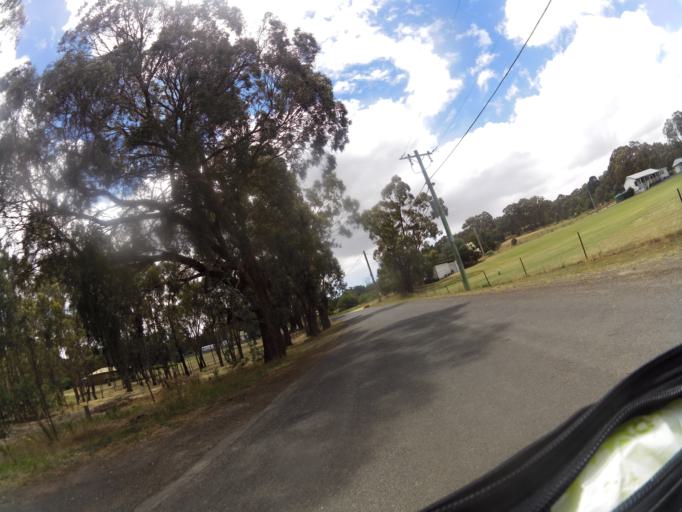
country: AU
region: Victoria
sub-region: Mount Alexander
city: Castlemaine
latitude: -37.0258
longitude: 144.2413
